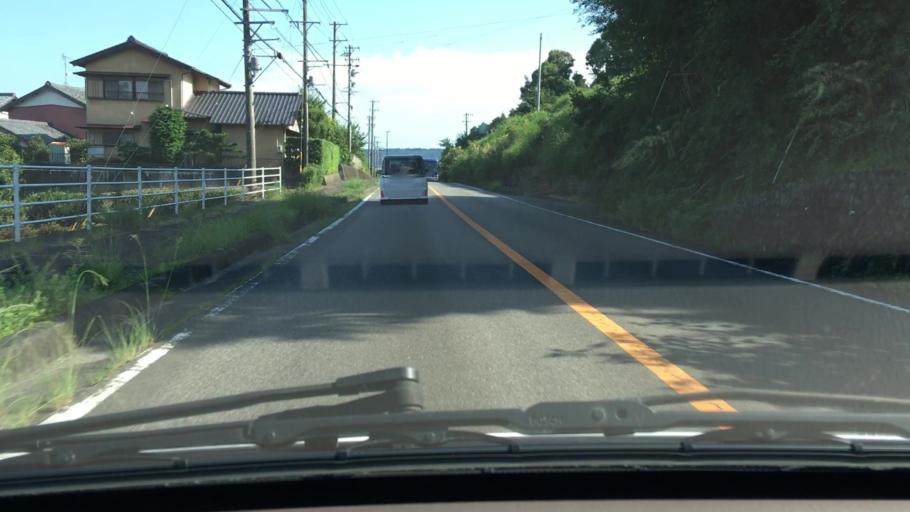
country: JP
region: Shizuoka
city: Kanaya
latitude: 34.8590
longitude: 138.1134
